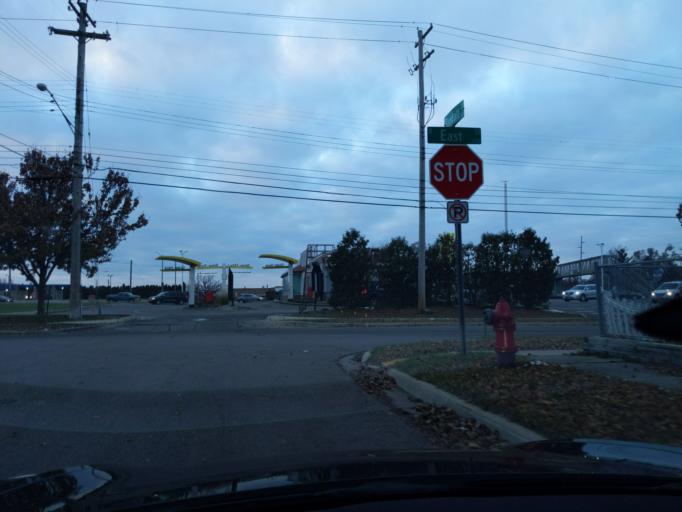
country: US
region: Michigan
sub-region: Ingham County
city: Lansing
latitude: 42.7569
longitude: -84.5426
